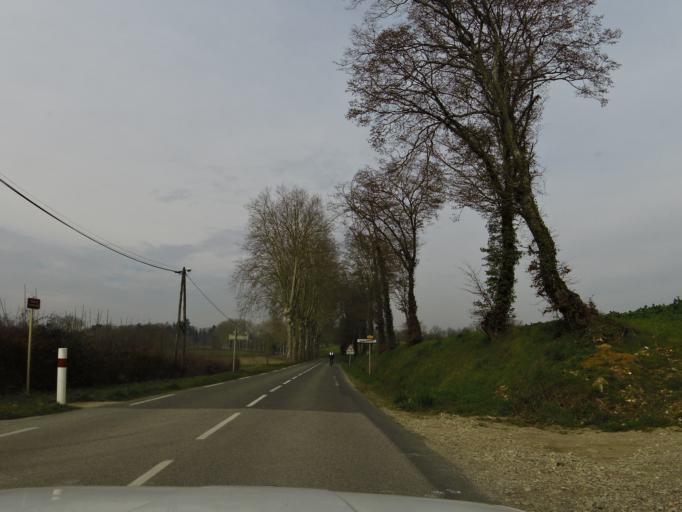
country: FR
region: Rhone-Alpes
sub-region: Departement de l'Ain
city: Chalamont
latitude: 45.9989
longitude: 5.1660
